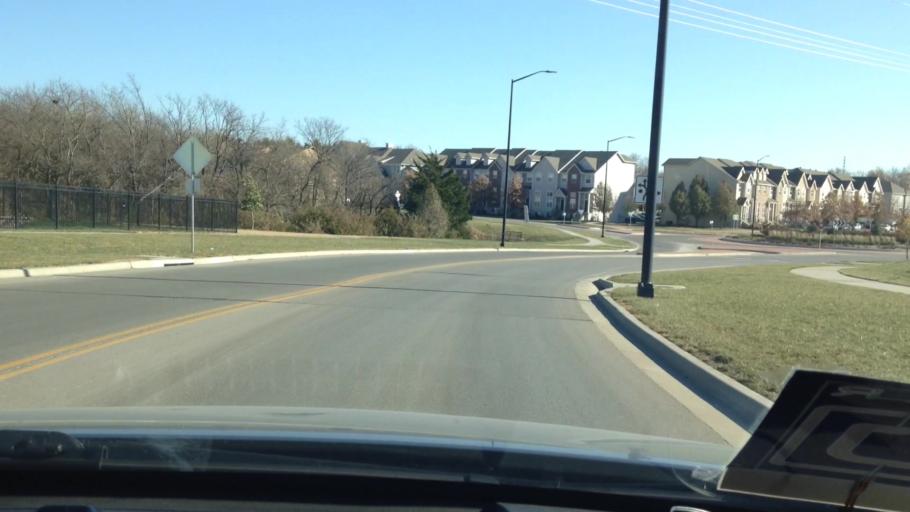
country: US
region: Kansas
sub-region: Johnson County
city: Olathe
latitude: 38.8866
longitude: -94.8514
